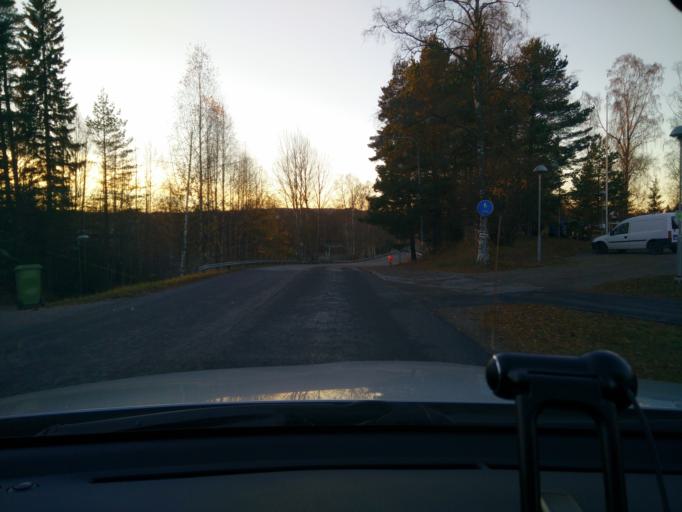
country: SE
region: Vaesternorrland
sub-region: Sundsvalls Kommun
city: Matfors
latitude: 62.3481
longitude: 17.0292
